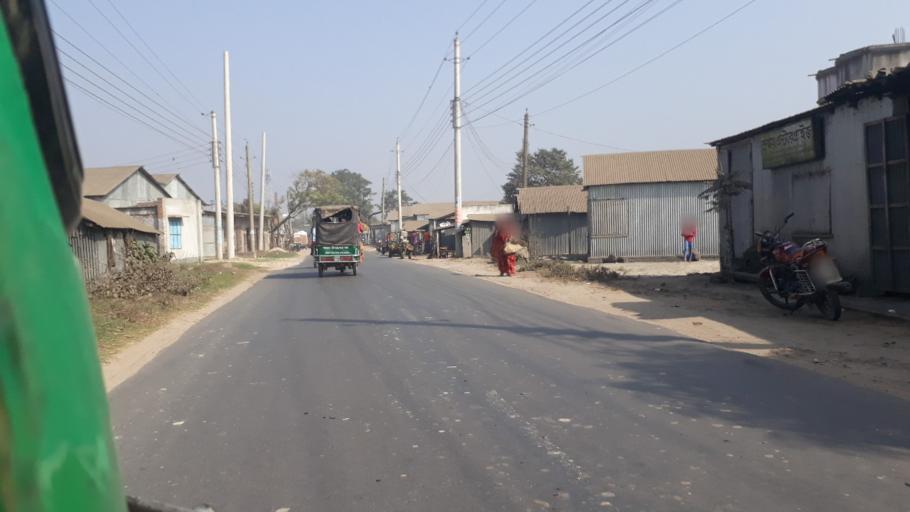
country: BD
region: Khulna
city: Kushtia
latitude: 23.8640
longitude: 89.0518
